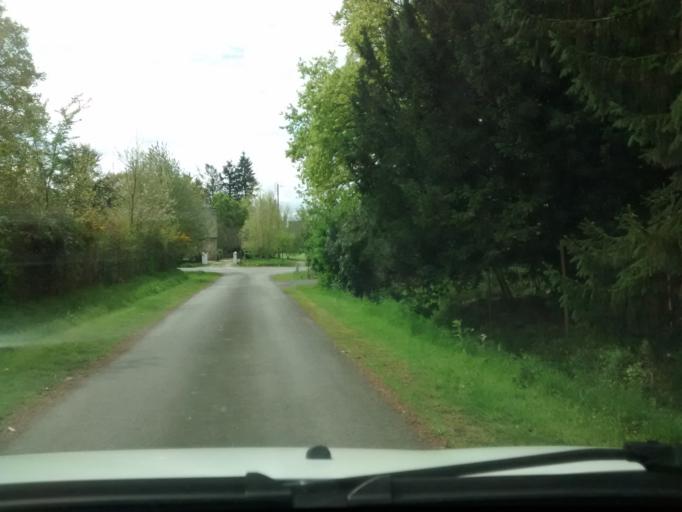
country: FR
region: Brittany
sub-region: Departement d'Ille-et-Vilaine
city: Noyal-sur-Vilaine
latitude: 48.0996
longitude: -1.5608
